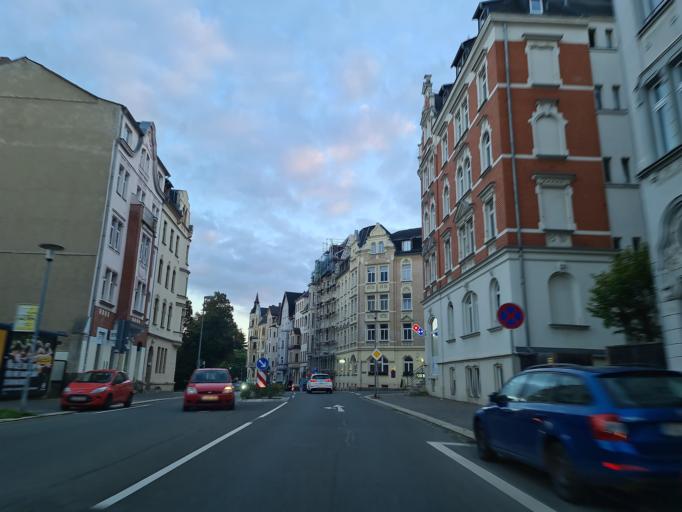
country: DE
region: Saxony
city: Plauen
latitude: 50.4935
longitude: 12.1233
